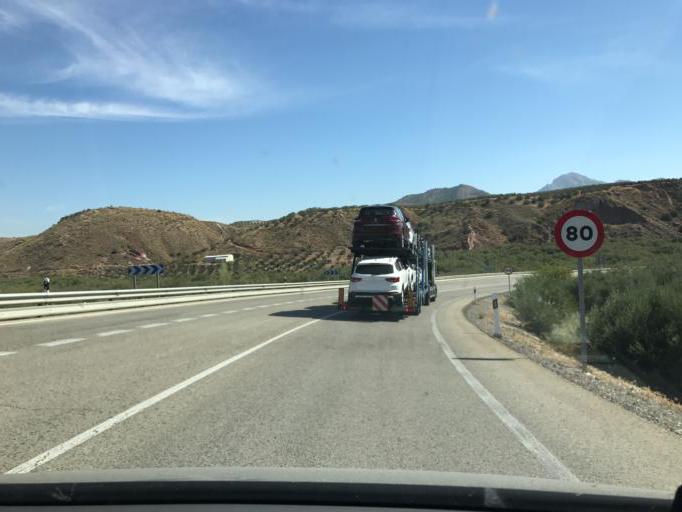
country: ES
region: Andalusia
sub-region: Province of Cordoba
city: Fuente-Tojar
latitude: 37.5795
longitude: -4.1631
